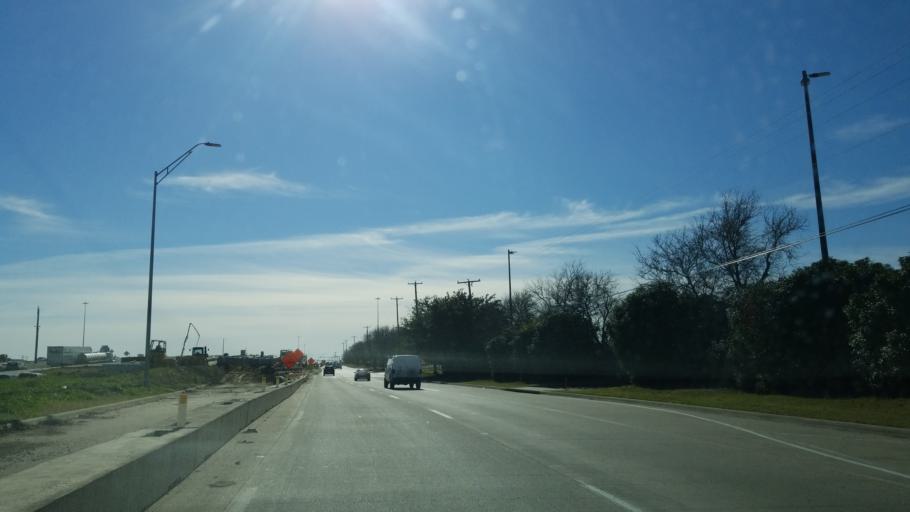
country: US
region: Texas
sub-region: Tarrant County
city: Arlington
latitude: 32.7407
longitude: -97.0630
